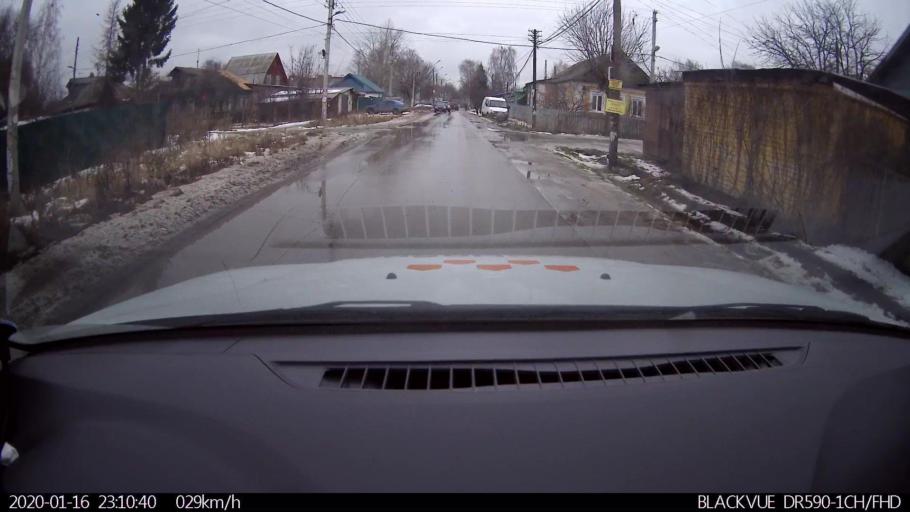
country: RU
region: Nizjnij Novgorod
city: Nizhniy Novgorod
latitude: 56.2875
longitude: 43.9027
